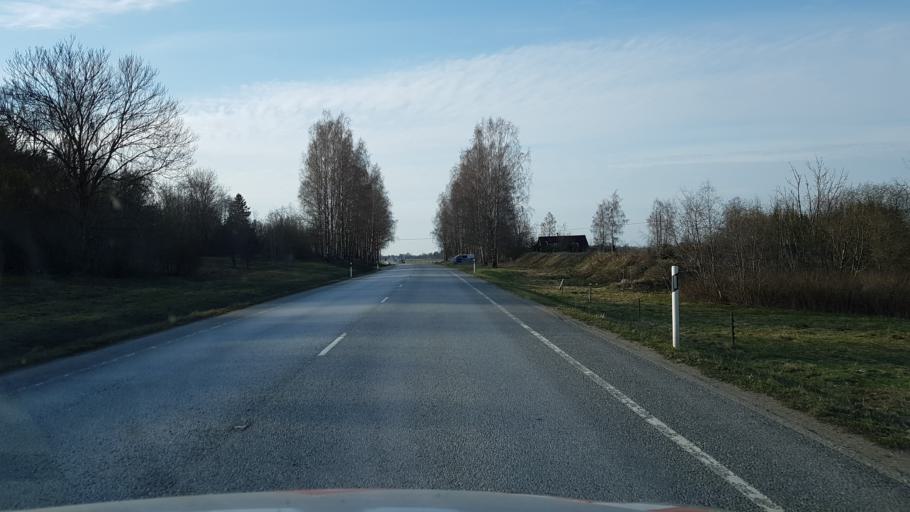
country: EE
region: Laeaene-Virumaa
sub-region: Haljala vald
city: Haljala
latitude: 59.4020
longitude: 26.3036
